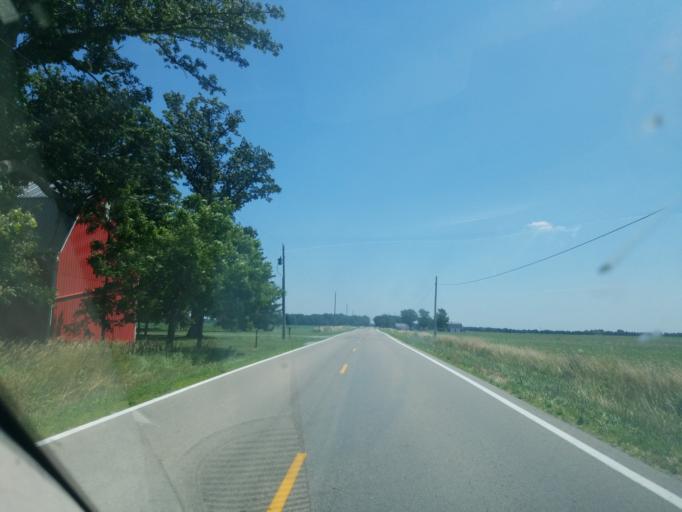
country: US
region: Ohio
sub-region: Allen County
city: Spencerville
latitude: 40.7426
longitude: -84.4492
